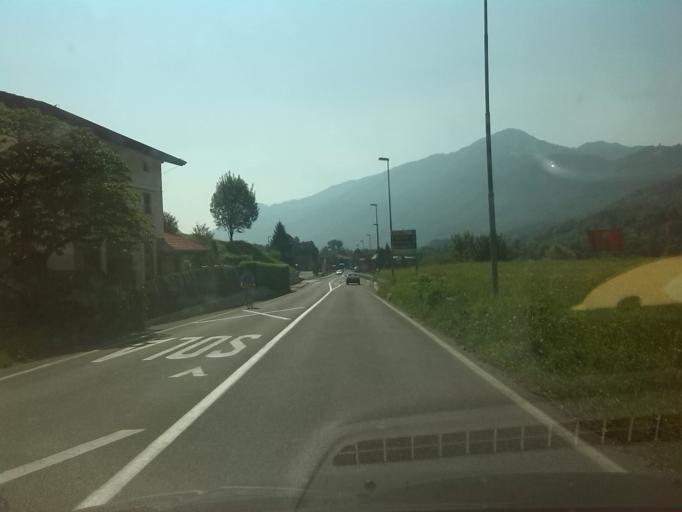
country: SI
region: Kobarid
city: Kobarid
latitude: 46.2437
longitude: 13.5800
